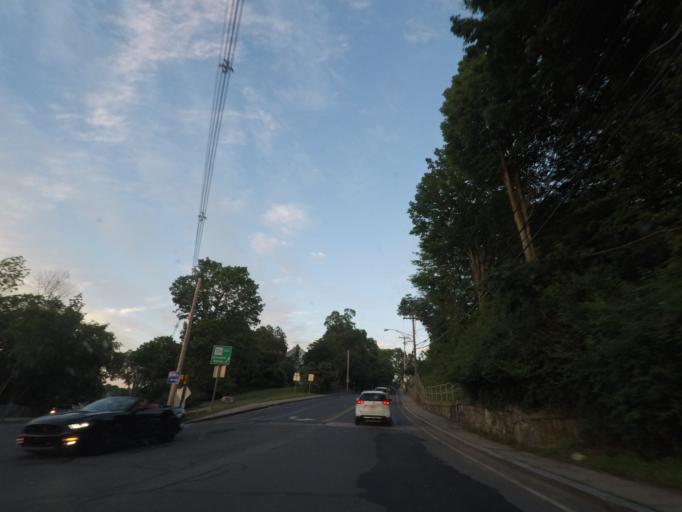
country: US
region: Massachusetts
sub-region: Worcester County
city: Southbridge
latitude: 42.0806
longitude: -72.0441
